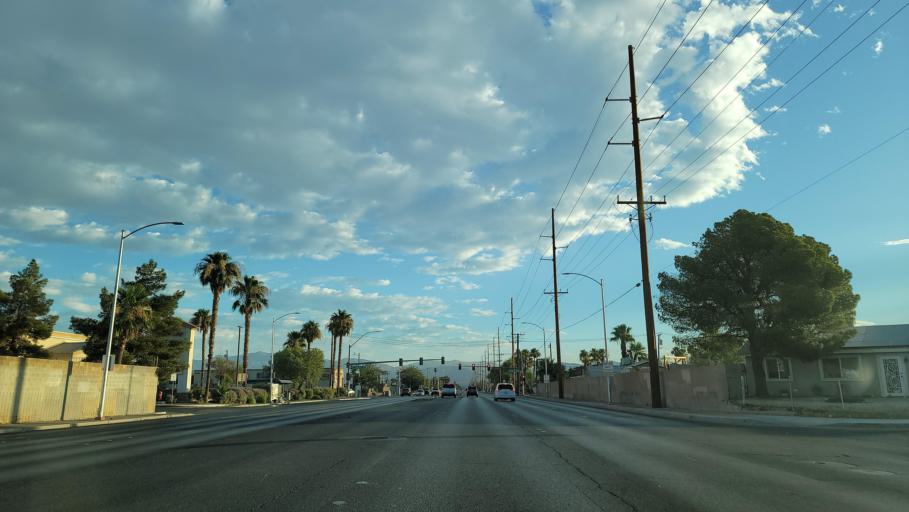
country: US
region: Nevada
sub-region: Clark County
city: North Las Vegas
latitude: 36.1869
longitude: -115.0983
